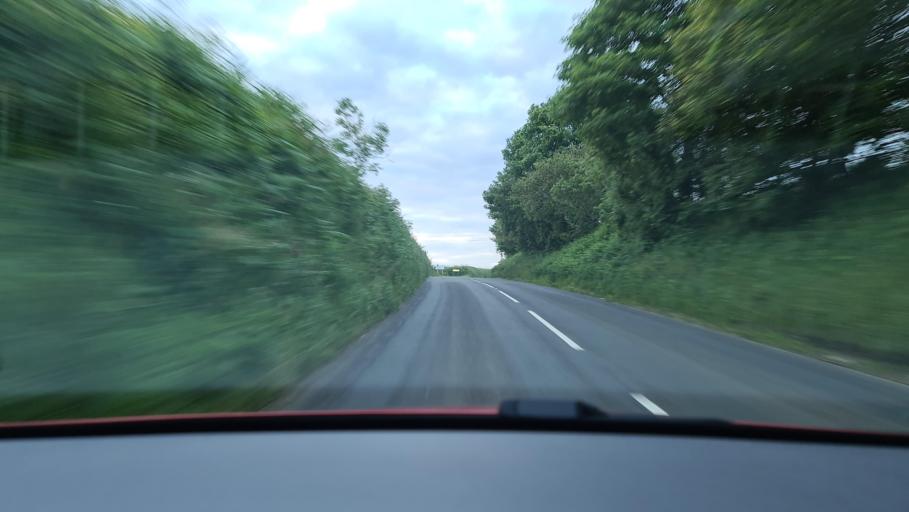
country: GB
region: England
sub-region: Cornwall
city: Liskeard
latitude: 50.4291
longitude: -4.4367
